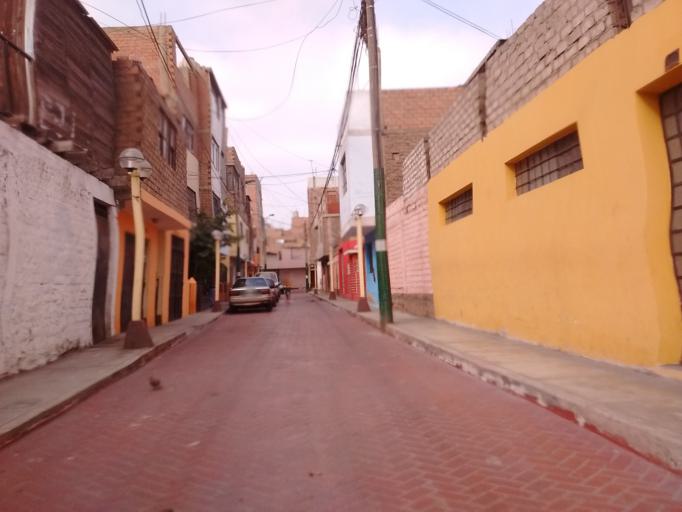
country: PE
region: Callao
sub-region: Callao
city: Callao
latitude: -12.0401
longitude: -77.0876
